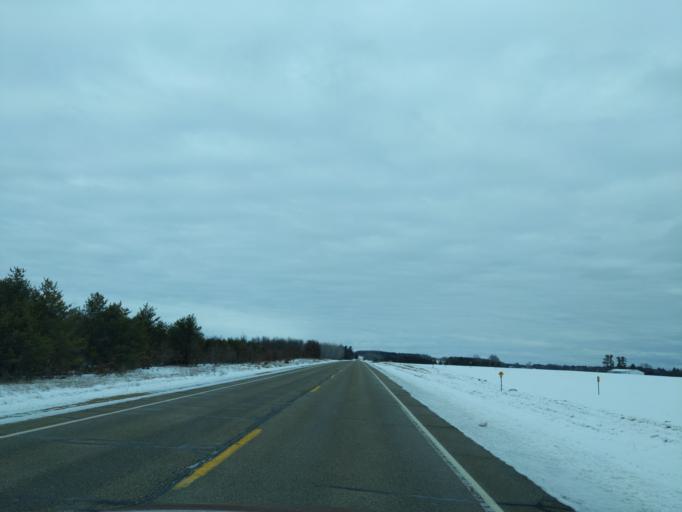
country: US
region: Wisconsin
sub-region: Waushara County
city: Wautoma
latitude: 43.9873
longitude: -89.3276
